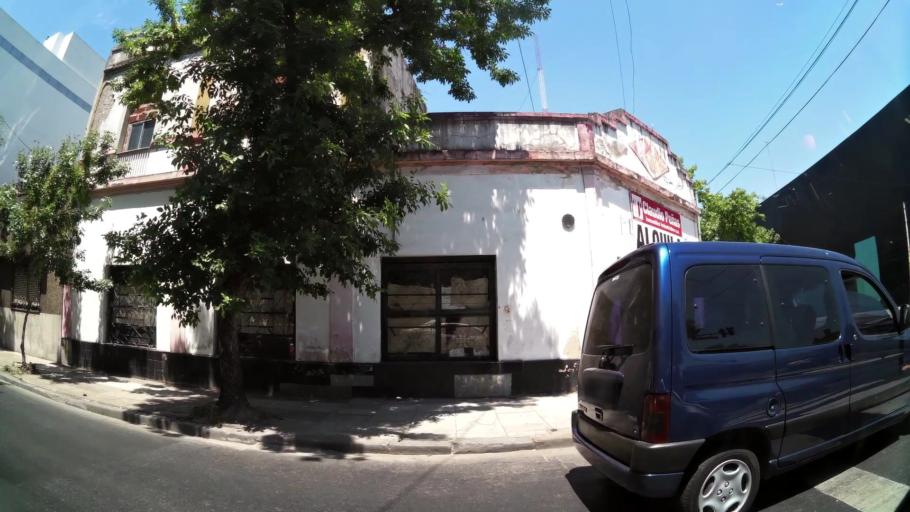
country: AR
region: Buenos Aires
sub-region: Partido de Avellaneda
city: Avellaneda
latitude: -34.6557
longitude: -58.3886
